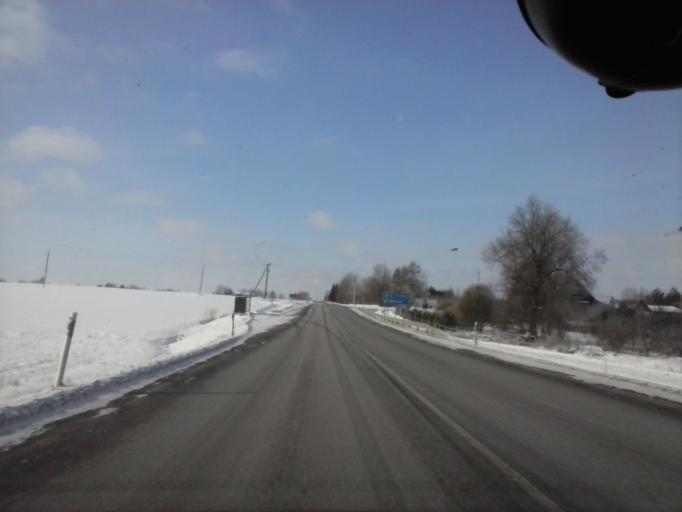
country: EE
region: Tartu
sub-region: Puhja vald
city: Puhja
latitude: 58.3454
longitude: 26.3967
